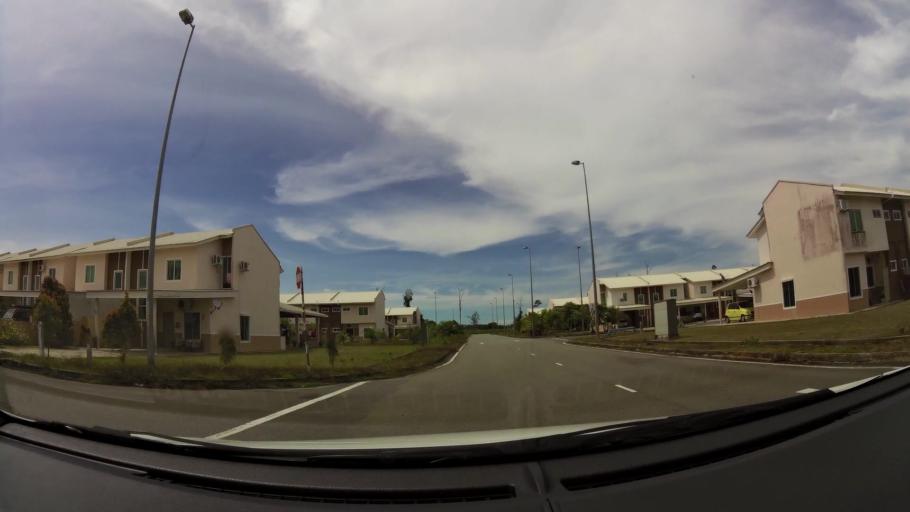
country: BN
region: Belait
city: Kuala Belait
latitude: 4.5918
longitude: 114.2787
